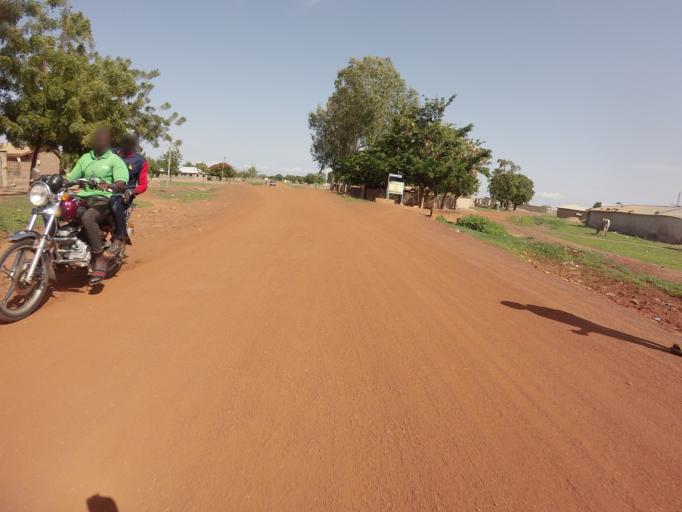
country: GH
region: Upper East
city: Bawku
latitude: 10.8393
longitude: -0.1785
